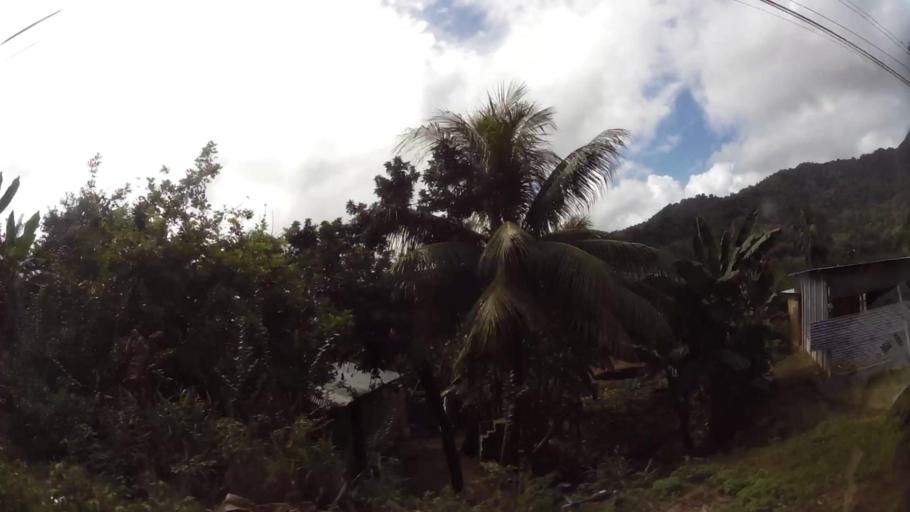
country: DM
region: Saint David
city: Castle Bruce
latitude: 15.4656
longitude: -61.2489
